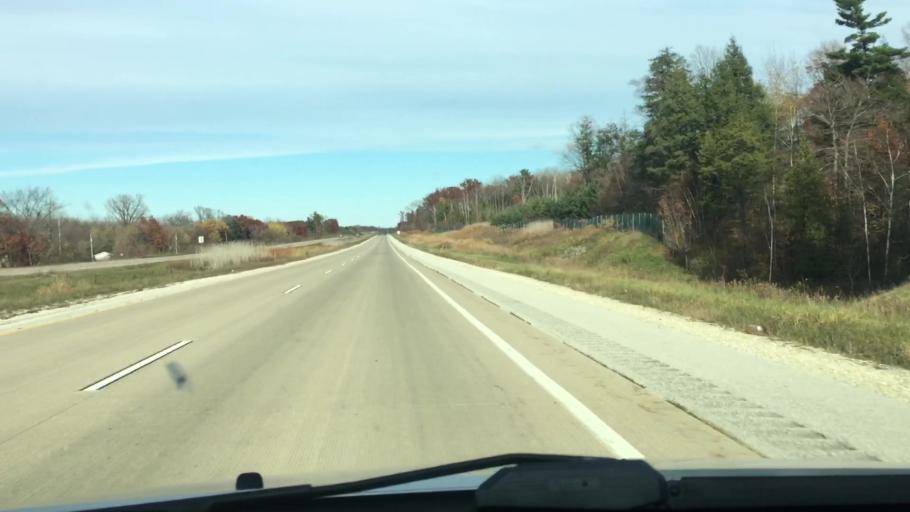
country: US
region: Wisconsin
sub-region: Kewaunee County
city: Luxemburg
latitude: 44.6893
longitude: -87.7188
